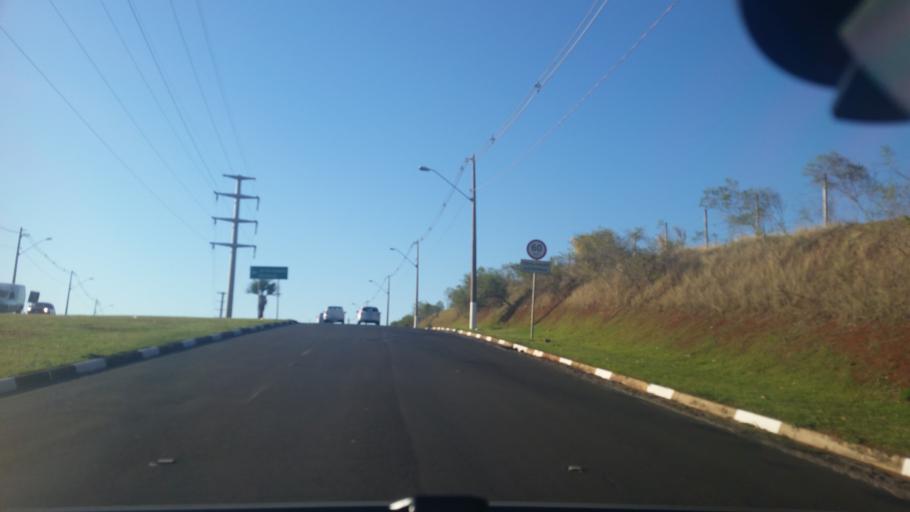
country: BR
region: Sao Paulo
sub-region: Campinas
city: Campinas
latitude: -22.8398
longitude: -47.0626
